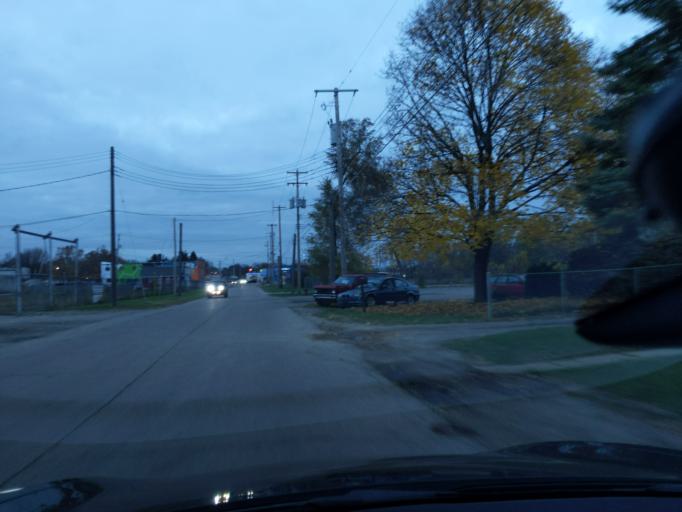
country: US
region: Michigan
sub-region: Ingham County
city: East Lansing
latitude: 42.7313
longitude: -84.5125
